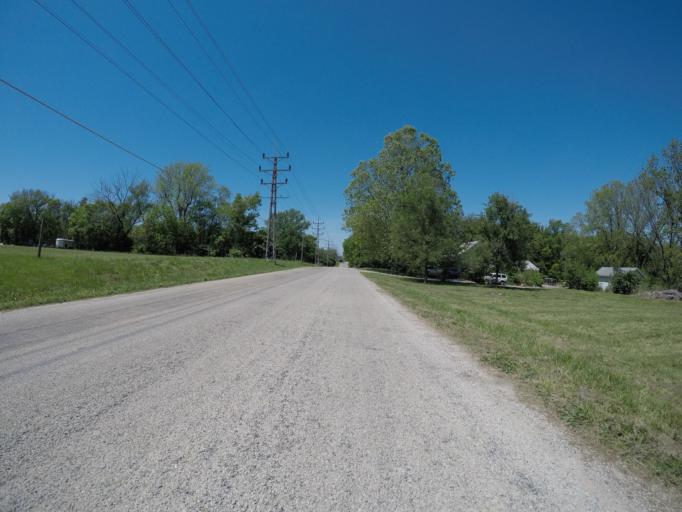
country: US
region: Kansas
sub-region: Shawnee County
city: Topeka
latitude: 39.0516
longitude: -95.6196
